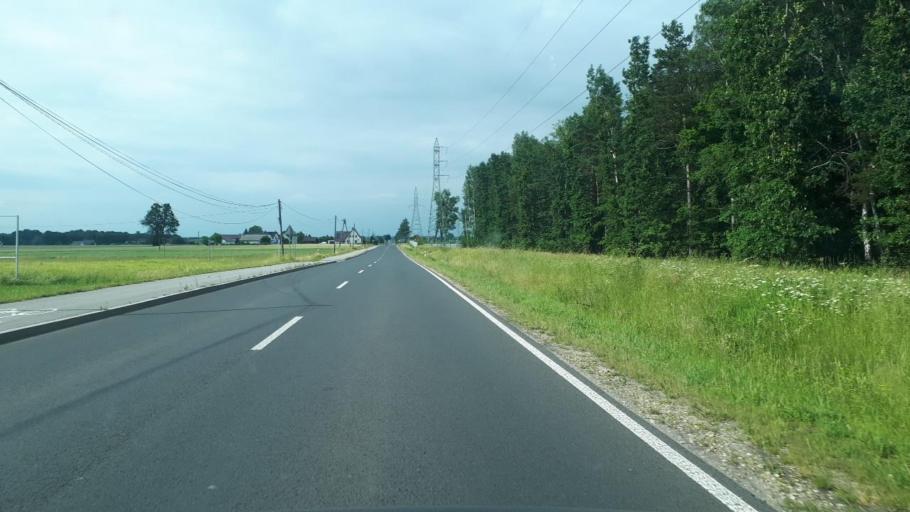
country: PL
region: Opole Voivodeship
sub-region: Powiat oleski
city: Olesno
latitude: 50.8420
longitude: 18.4127
